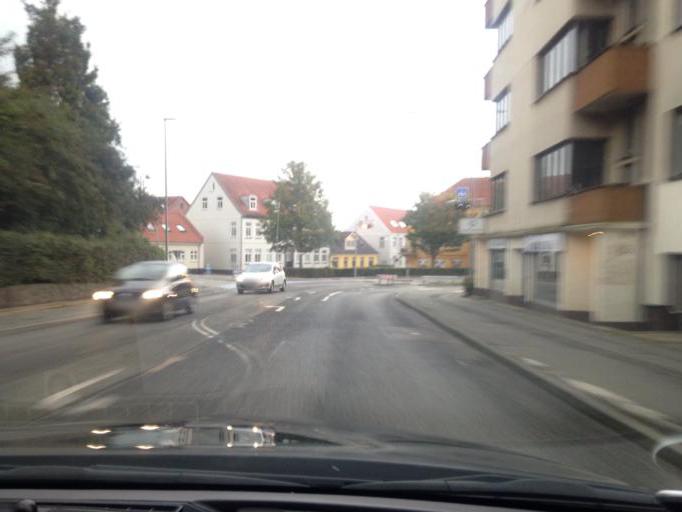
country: DK
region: South Denmark
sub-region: Kolding Kommune
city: Kolding
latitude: 55.4943
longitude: 9.4642
